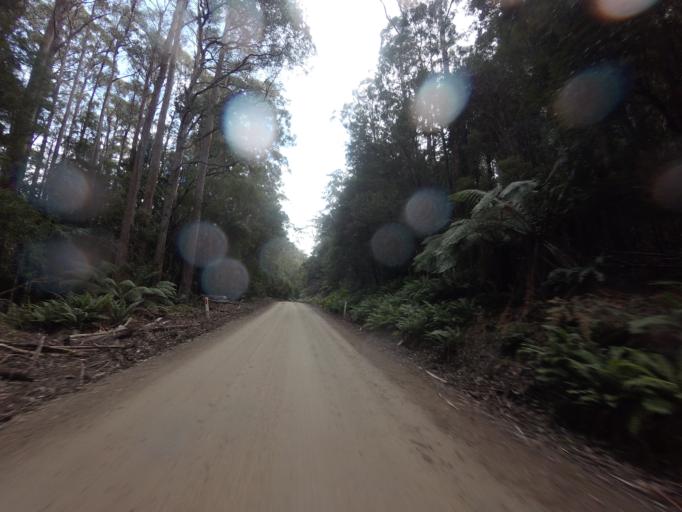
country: AU
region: Tasmania
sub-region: Huon Valley
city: Geeveston
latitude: -43.3932
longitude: 146.8553
